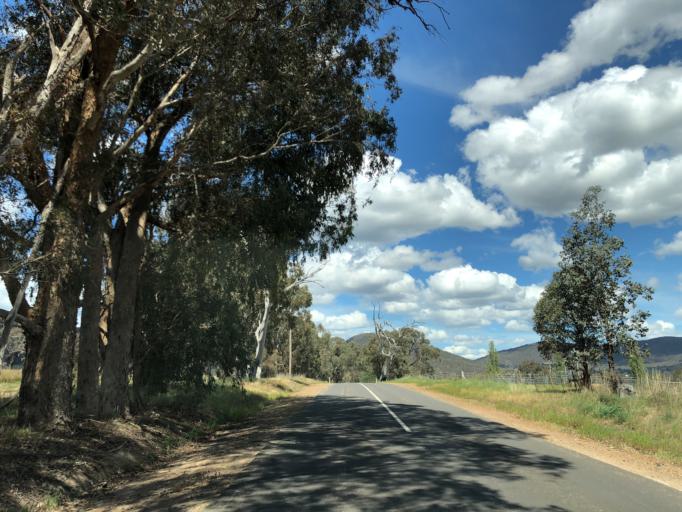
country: AU
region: Victoria
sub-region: Benalla
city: Benalla
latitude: -36.7422
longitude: 146.1170
